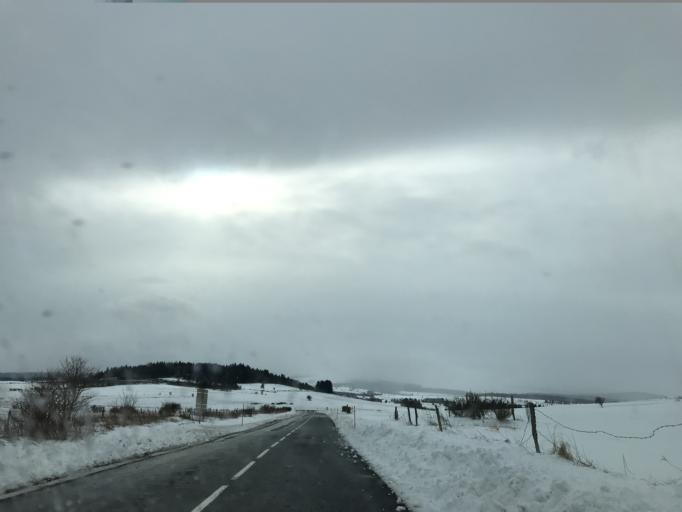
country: FR
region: Auvergne
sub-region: Departement du Puy-de-Dome
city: Aydat
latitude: 45.6680
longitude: 2.9374
